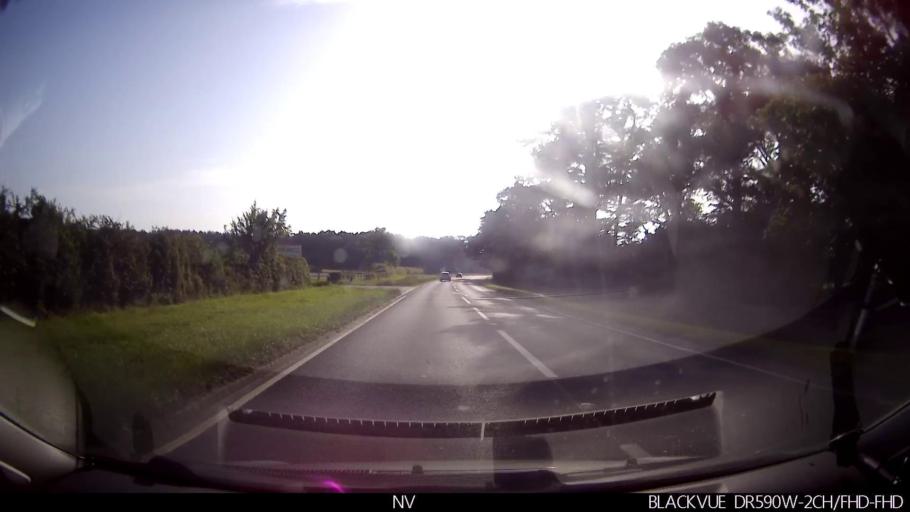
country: GB
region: England
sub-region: North Yorkshire
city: Wintringham
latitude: 54.1664
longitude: -0.6542
